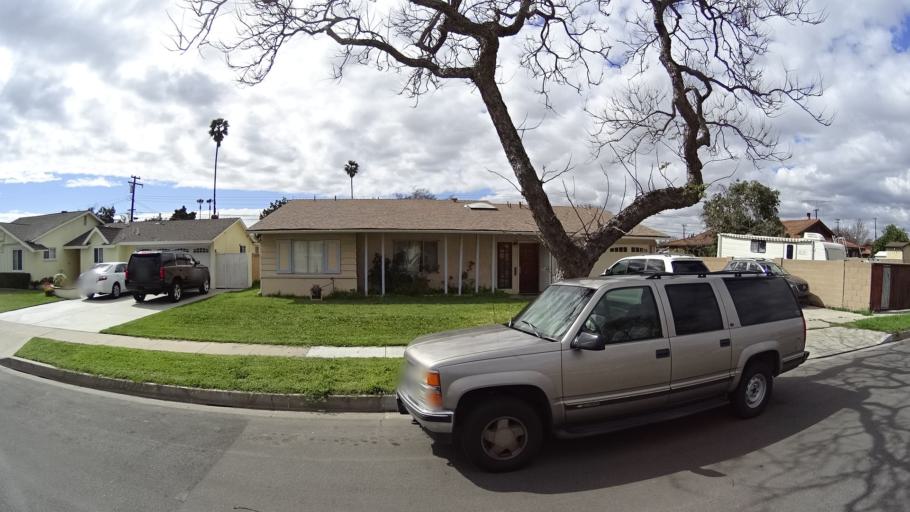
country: US
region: California
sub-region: Orange County
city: Anaheim
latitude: 33.8241
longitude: -117.9554
